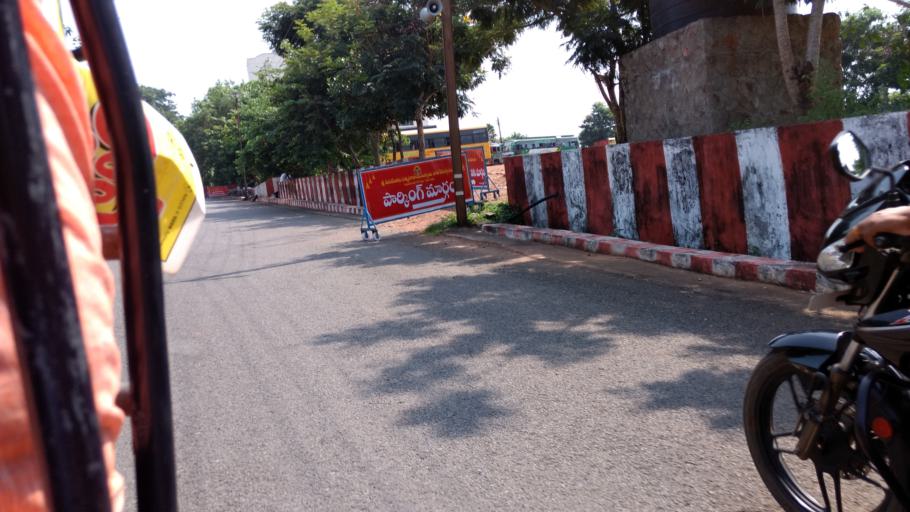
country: IN
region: Andhra Pradesh
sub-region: East Godavari
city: Tuni
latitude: 17.2812
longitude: 82.3982
